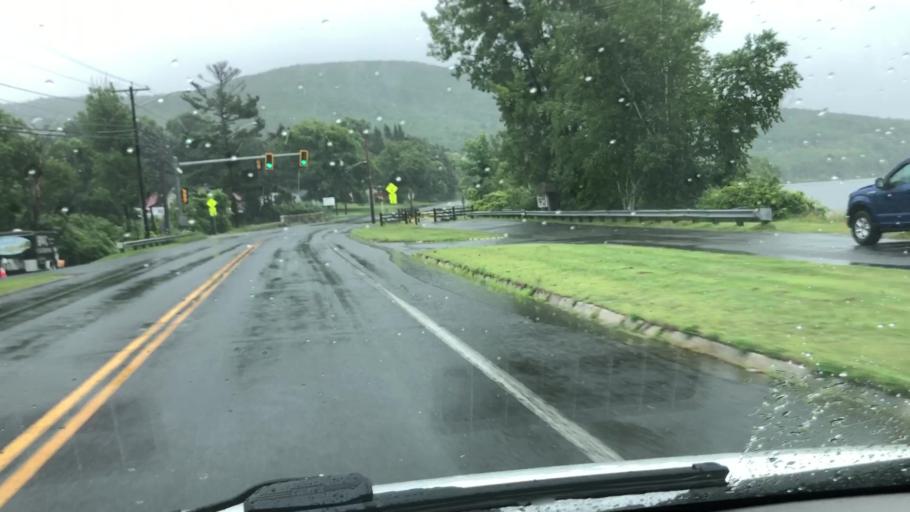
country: US
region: Massachusetts
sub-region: Berkshire County
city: Lanesborough
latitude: 42.5547
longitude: -73.1656
